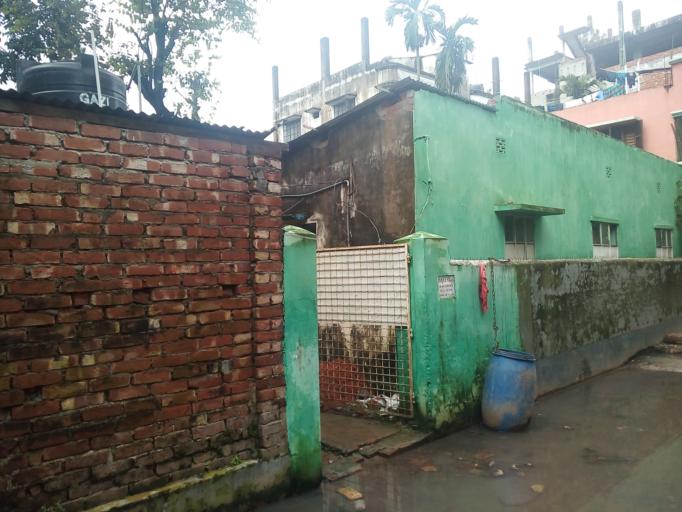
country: BD
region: Dhaka
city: Tungi
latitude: 23.8417
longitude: 90.2526
